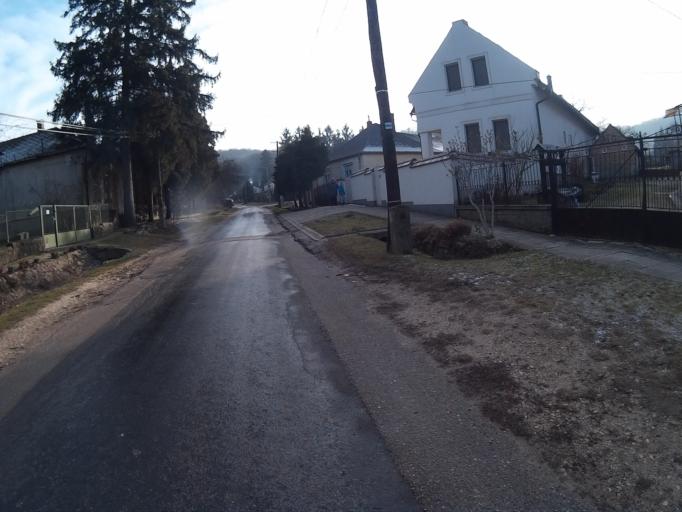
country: HU
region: Komarom-Esztergom
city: Oroszlany
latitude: 47.4729
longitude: 18.3980
